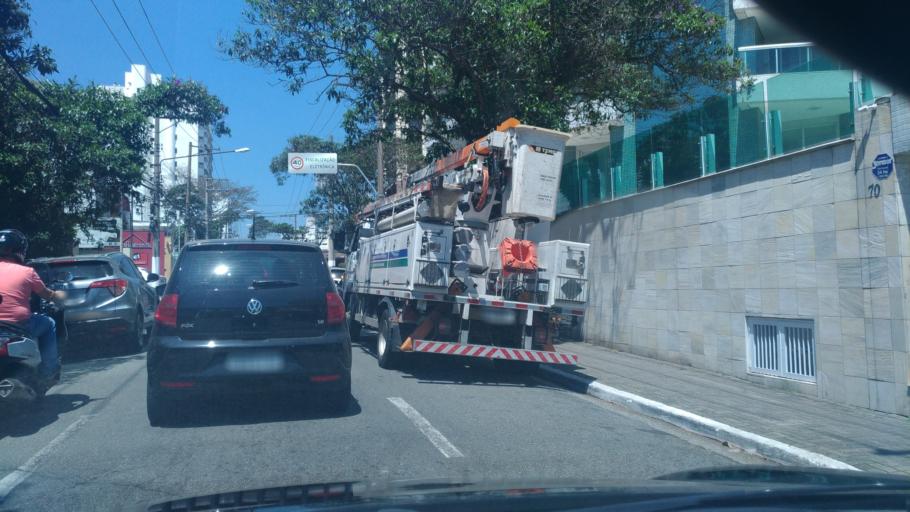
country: BR
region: Sao Paulo
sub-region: Sao Bernardo Do Campo
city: Sao Bernardo do Campo
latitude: -23.7081
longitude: -46.5489
